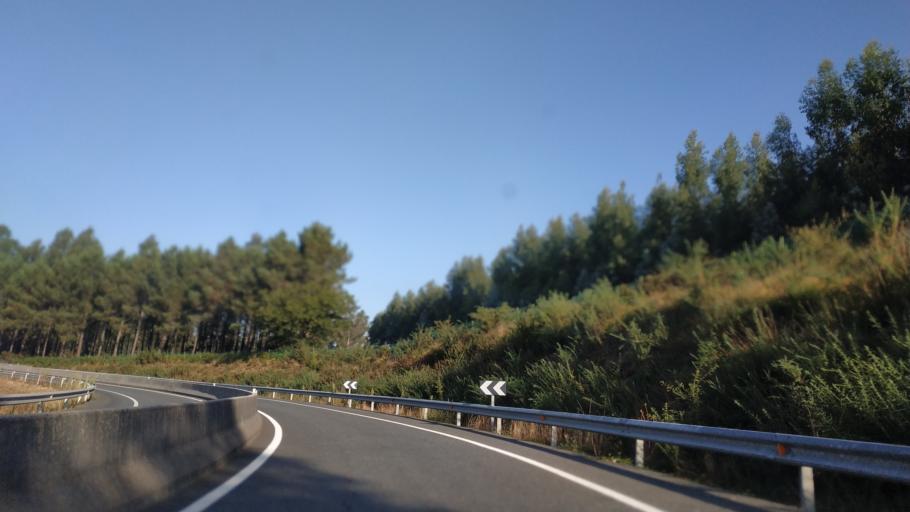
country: ES
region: Galicia
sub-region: Provincia da Coruna
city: Carballo
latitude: 43.2463
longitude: -8.6717
